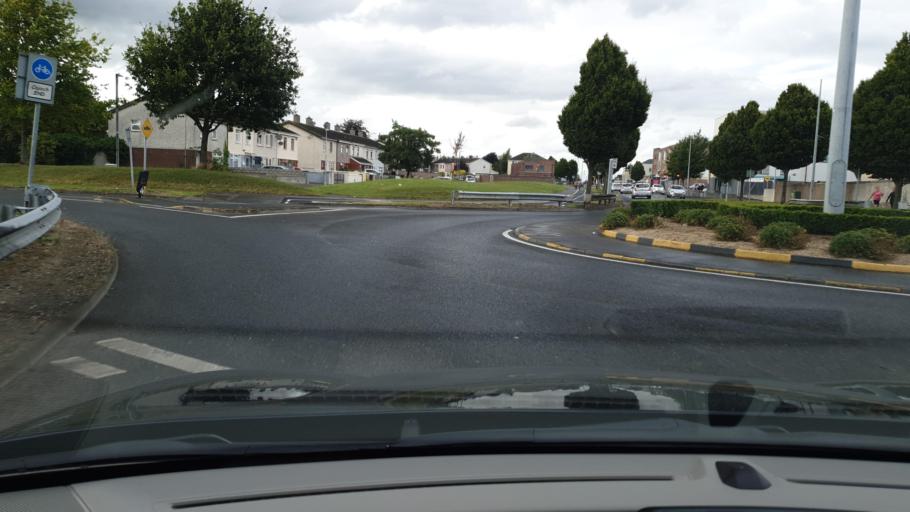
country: IE
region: Leinster
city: Clondalkin
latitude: 53.3426
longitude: -6.3988
